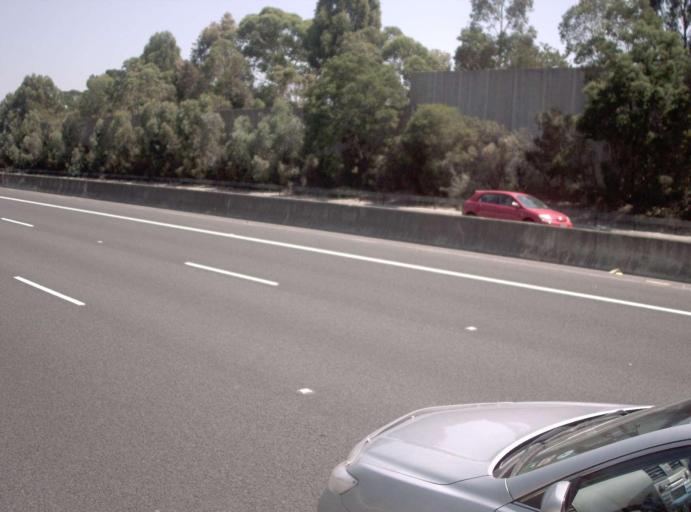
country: AU
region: Victoria
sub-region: Whitehorse
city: Blackburn North
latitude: -37.7999
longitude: 145.1482
